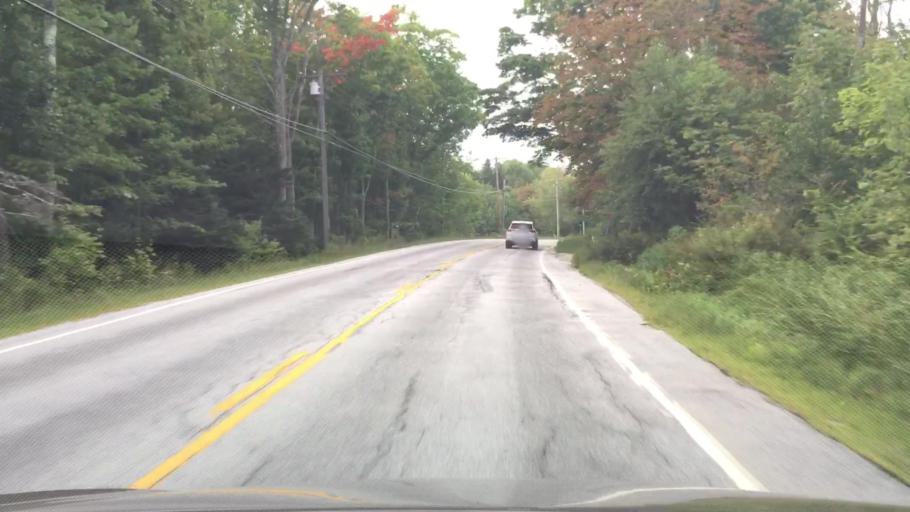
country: US
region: Maine
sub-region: Hancock County
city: Penobscot
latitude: 44.4313
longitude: -68.6055
